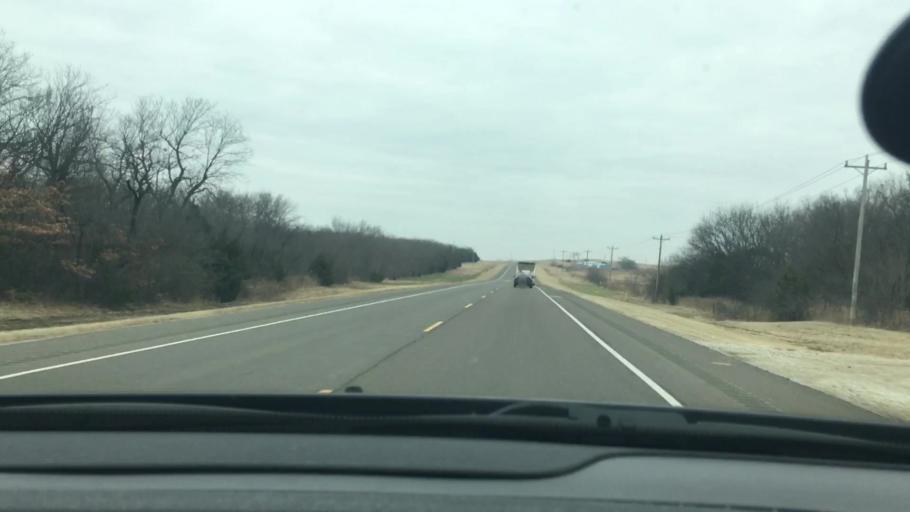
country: US
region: Oklahoma
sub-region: Murray County
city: Davis
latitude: 34.5158
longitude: -97.2046
